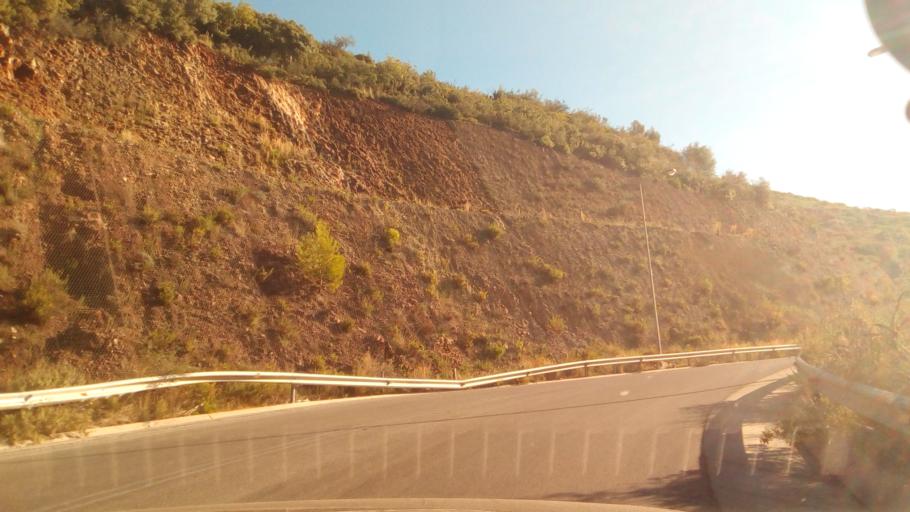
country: GR
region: West Greece
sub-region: Nomos Aitolias kai Akarnanias
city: Nafpaktos
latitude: 38.4139
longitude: 21.8424
